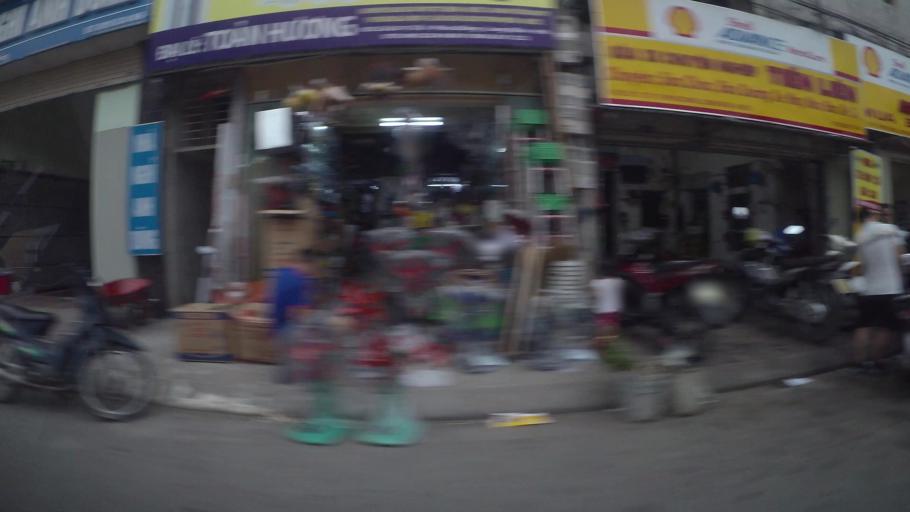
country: VN
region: Ha Noi
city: Trau Quy
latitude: 21.0395
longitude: 105.9028
